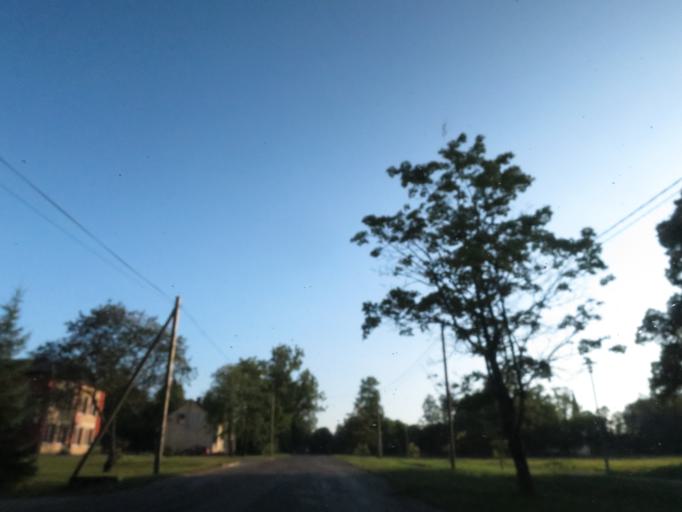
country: LV
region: Sigulda
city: Sigulda
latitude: 57.1634
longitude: 24.8578
